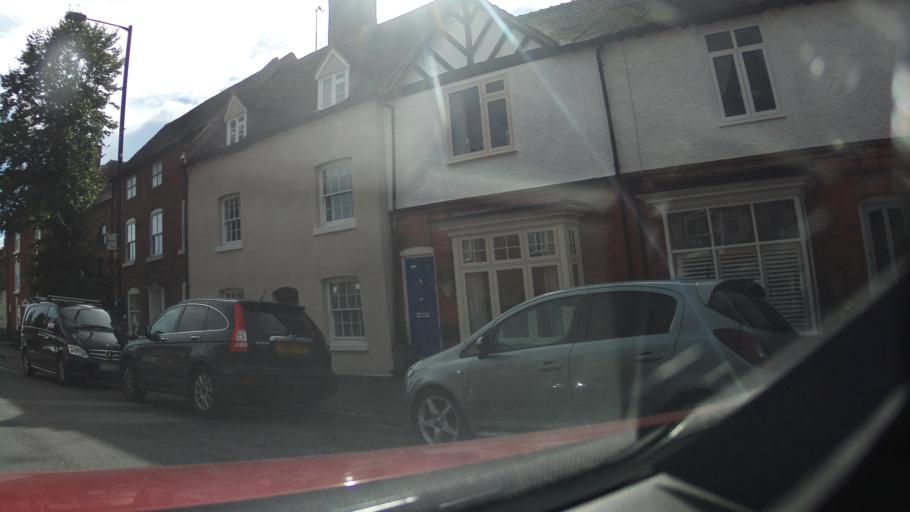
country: GB
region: England
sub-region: Shropshire
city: Shifnal
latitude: 52.6695
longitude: -2.3729
